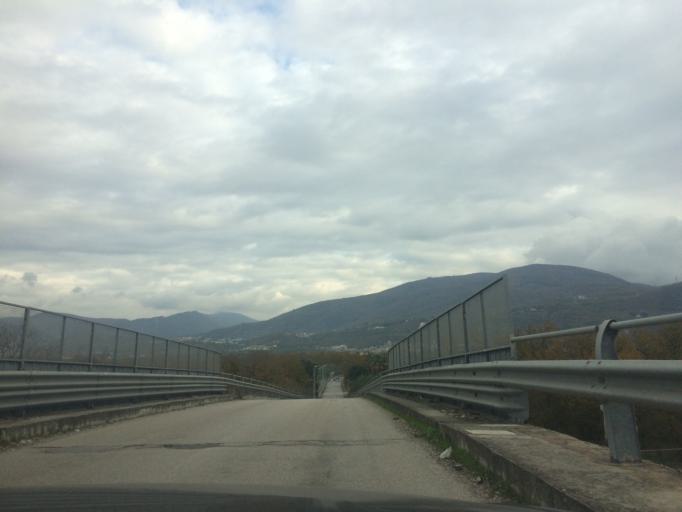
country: IT
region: Campania
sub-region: Provincia di Napoli
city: San Gennaro Vesuviano
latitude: 40.8732
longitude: 14.5361
